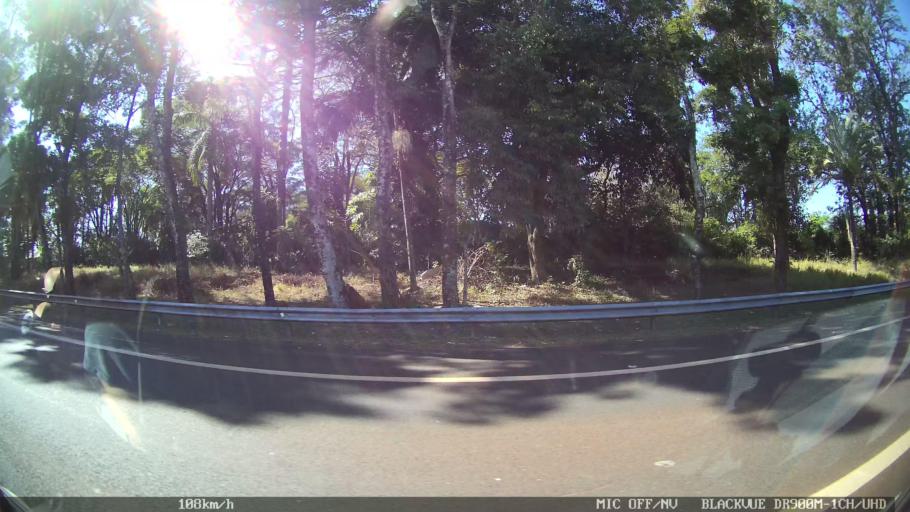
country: BR
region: Sao Paulo
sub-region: Batatais
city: Batatais
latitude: -20.8488
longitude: -47.6011
